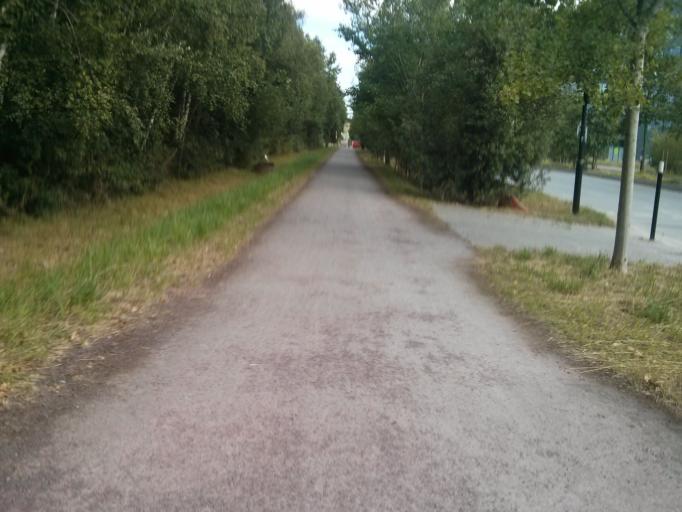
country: FR
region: Brittany
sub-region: Departement d'Ille-et-Vilaine
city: Saint-Jacques-de-la-Lande
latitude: 48.0952
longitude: -1.7065
